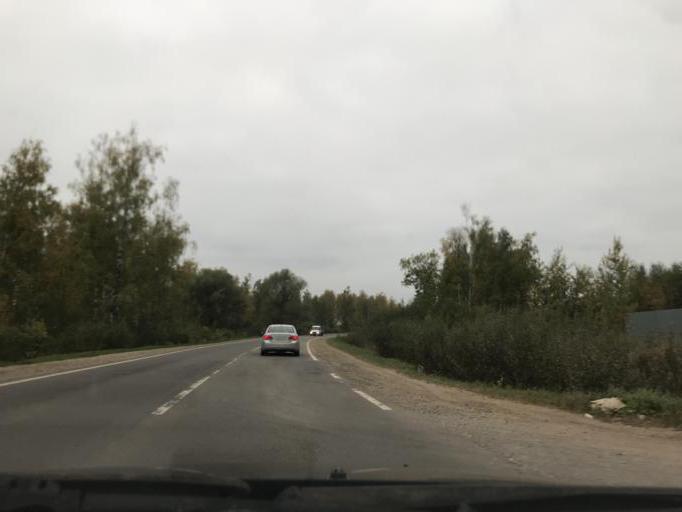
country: RU
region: Kaluga
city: Kaluga
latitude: 54.6171
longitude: 36.2832
